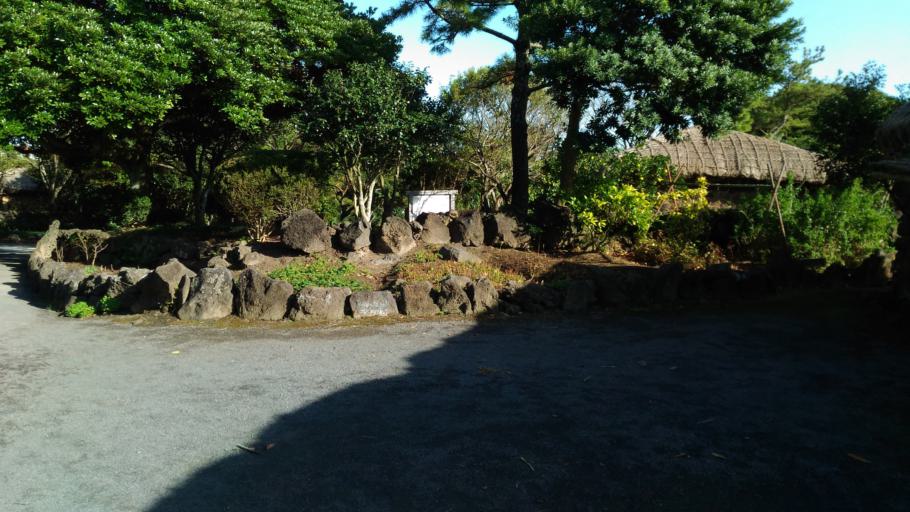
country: KR
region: Jeju-do
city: Seogwipo
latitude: 33.3215
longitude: 126.8404
